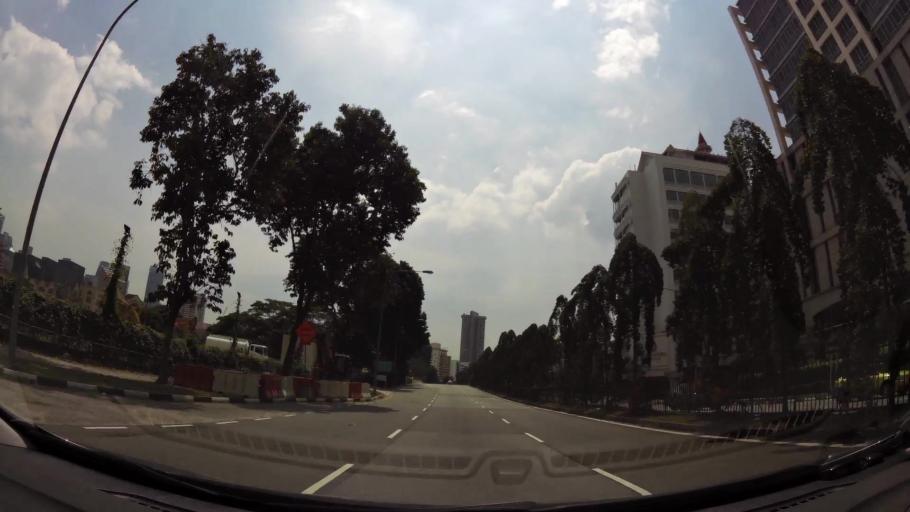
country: SG
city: Singapore
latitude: 1.2919
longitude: 103.8431
